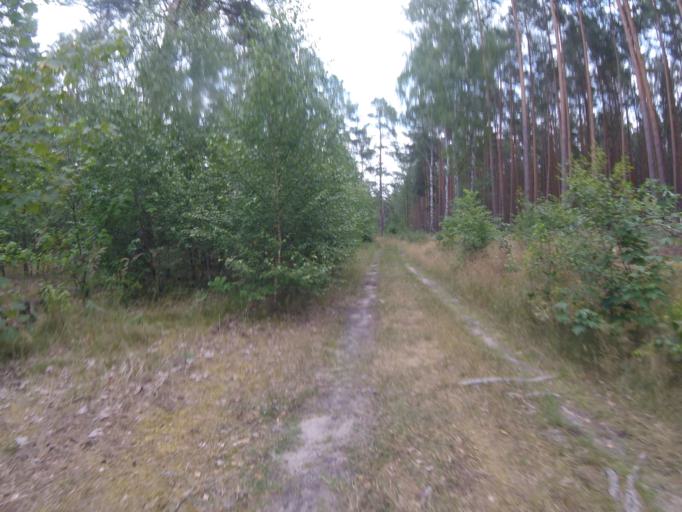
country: DE
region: Brandenburg
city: Schwerin
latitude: 52.1874
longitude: 13.6071
